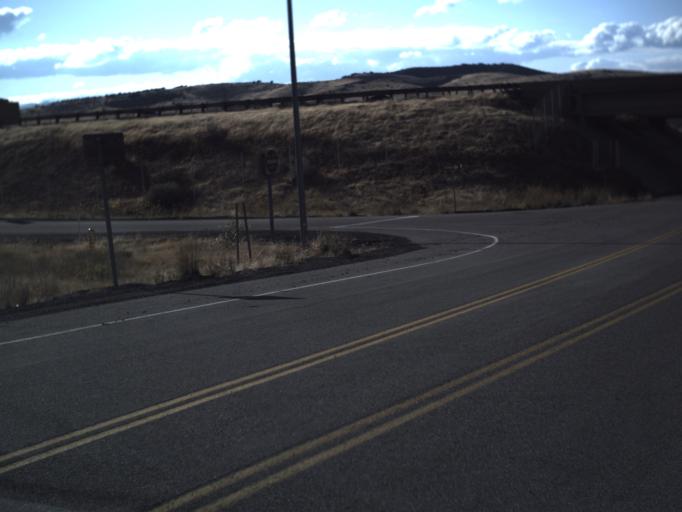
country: US
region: Utah
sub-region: Utah County
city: Santaquin
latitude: 39.9501
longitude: -111.8015
